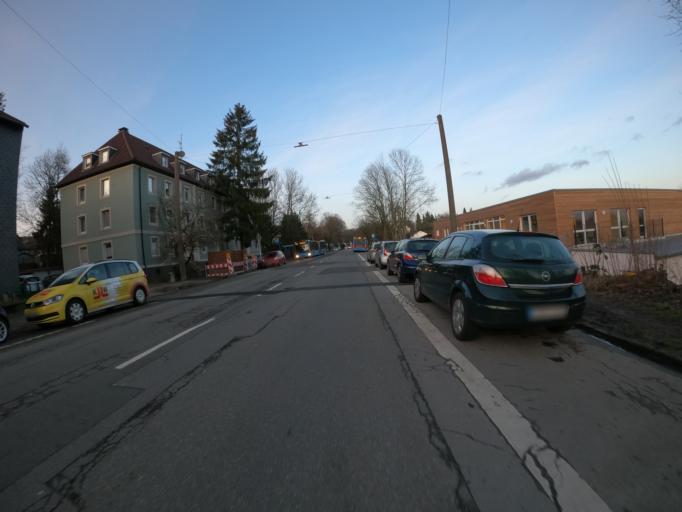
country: DE
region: North Rhine-Westphalia
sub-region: Regierungsbezirk Dusseldorf
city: Wuppertal
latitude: 51.2311
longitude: 7.1505
